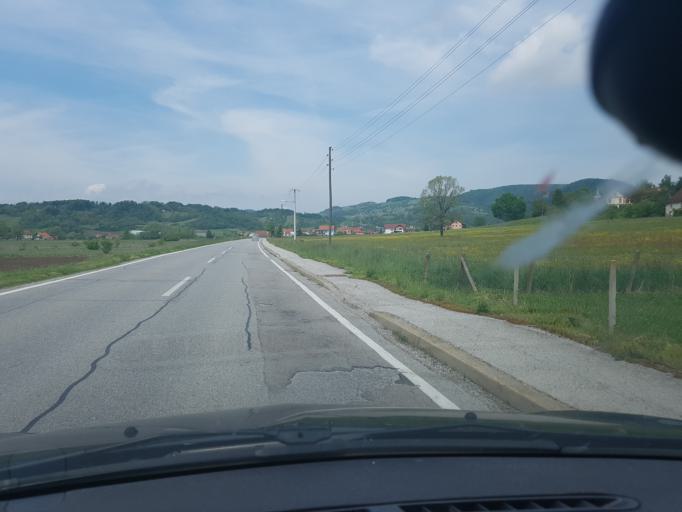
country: HR
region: Krapinsko-Zagorska
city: Pregrada
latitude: 46.1462
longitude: 15.7676
